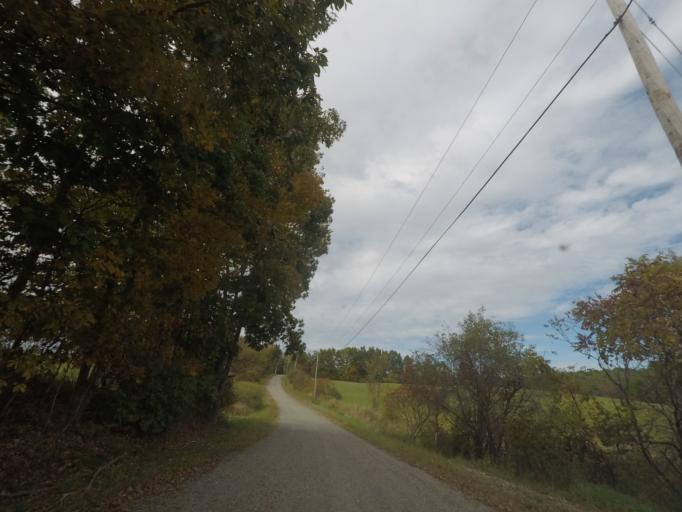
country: US
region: New York
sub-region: Rensselaer County
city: Nassau
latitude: 42.5796
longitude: -73.6129
